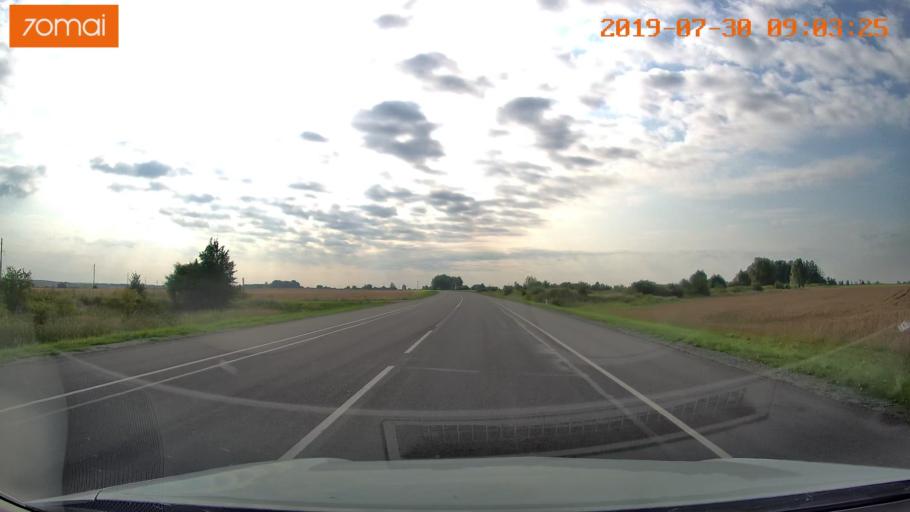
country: RU
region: Kaliningrad
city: Gusev
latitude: 54.6080
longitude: 22.2528
